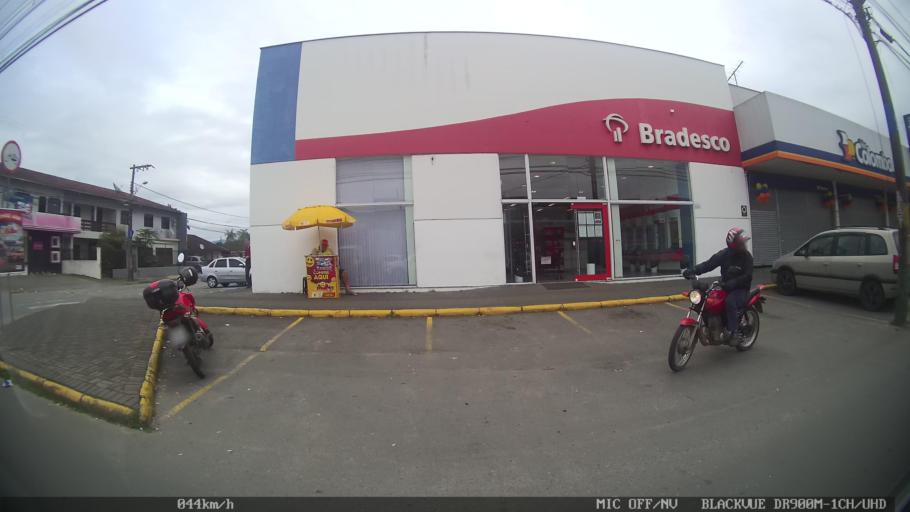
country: BR
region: Santa Catarina
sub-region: Joinville
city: Joinville
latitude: -26.2678
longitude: -48.8723
